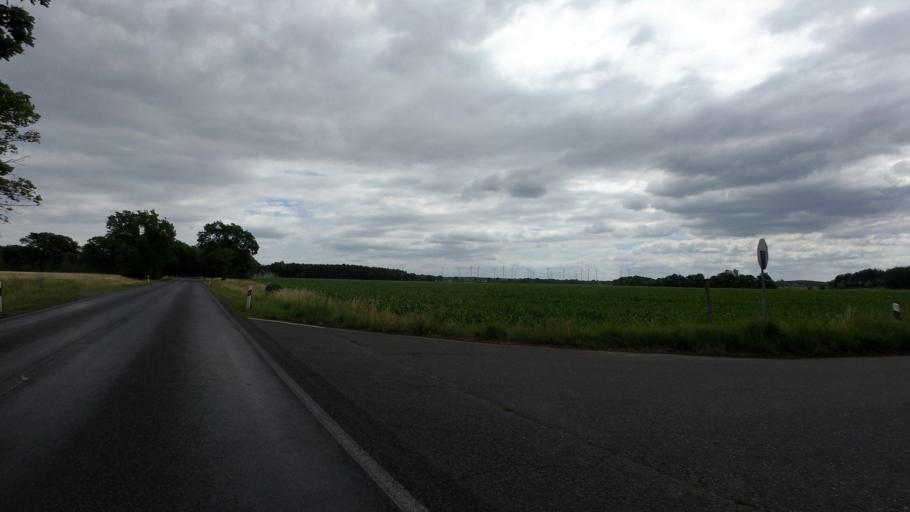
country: DE
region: Brandenburg
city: Calau
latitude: 51.7886
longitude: 13.8691
